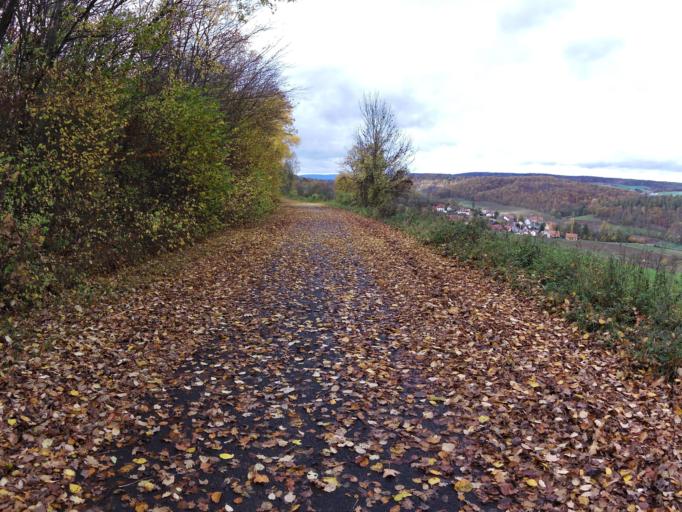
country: DE
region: Thuringia
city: Ifta
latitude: 51.0680
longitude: 10.1390
